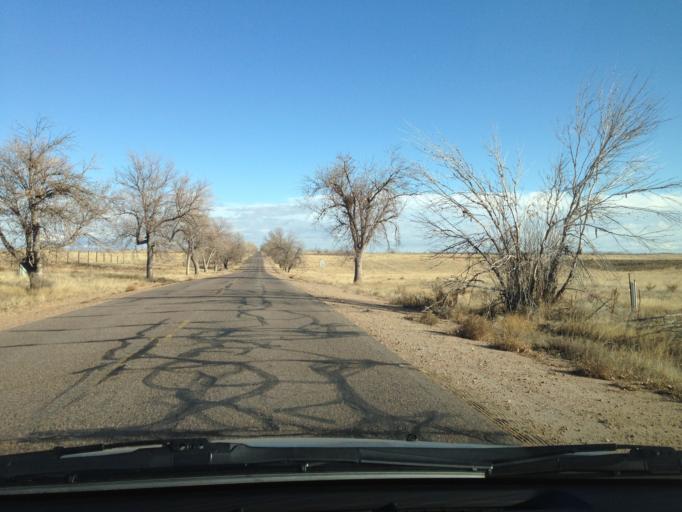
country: US
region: Colorado
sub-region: Adams County
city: Derby
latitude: 39.8272
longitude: -104.8830
